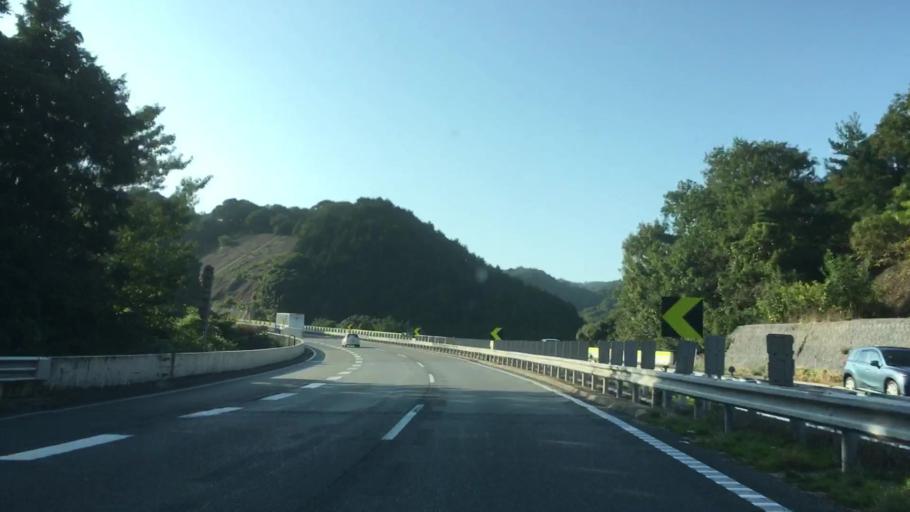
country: JP
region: Yamaguchi
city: Ogori-shimogo
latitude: 34.1360
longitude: 131.3736
